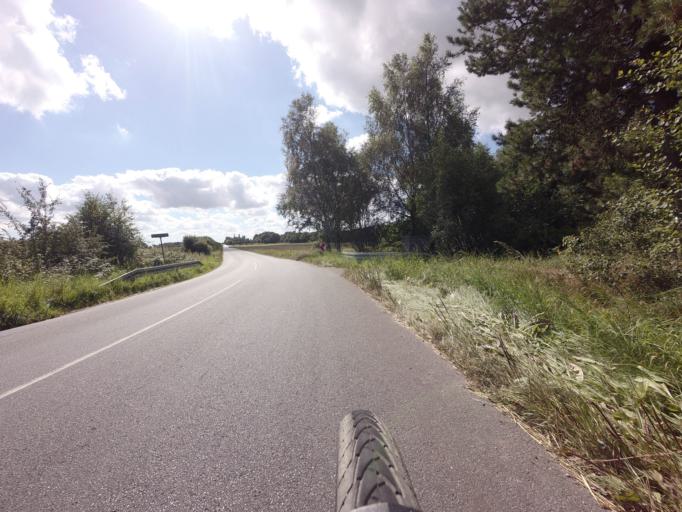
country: DK
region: Central Jutland
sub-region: Ikast-Brande Kommune
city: Brande
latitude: 55.9786
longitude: 9.1436
